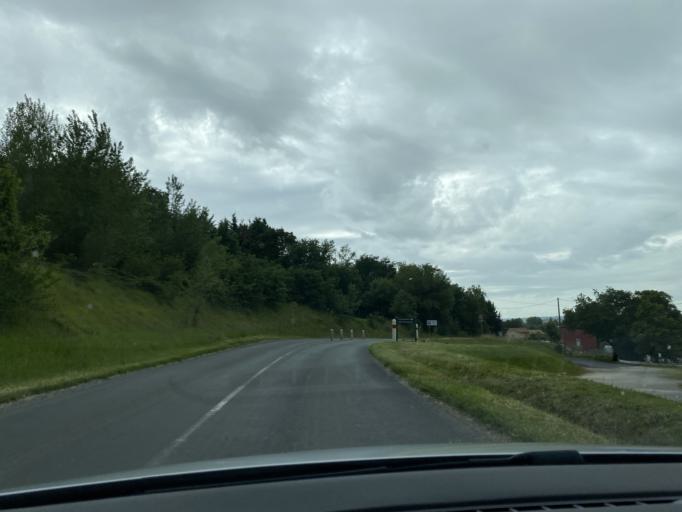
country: FR
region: Midi-Pyrenees
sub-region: Departement du Tarn
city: Saix
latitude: 43.5806
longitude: 2.1807
